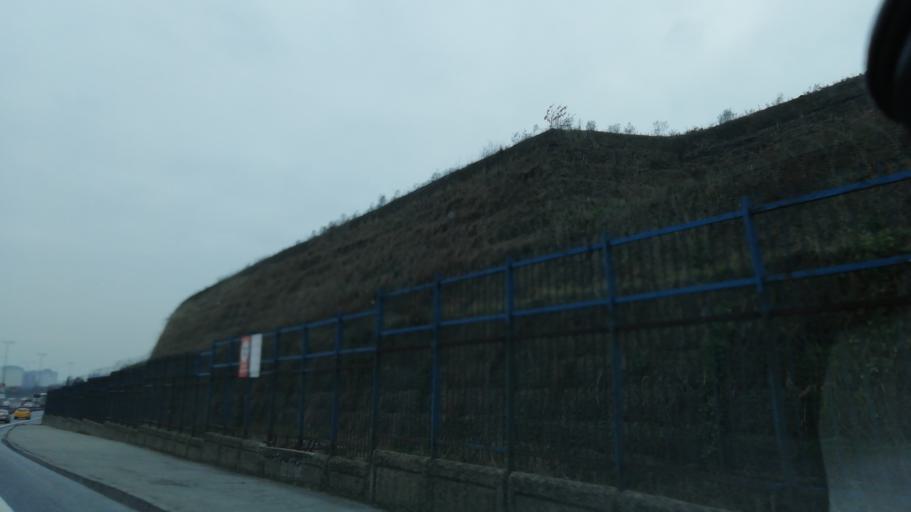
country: TR
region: Istanbul
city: Bahcelievler
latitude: 40.9994
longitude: 28.8102
